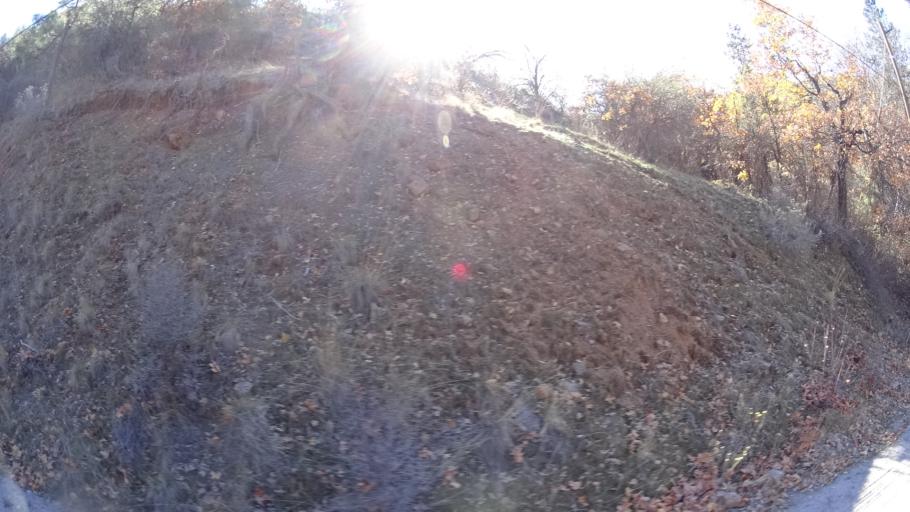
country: US
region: California
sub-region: Siskiyou County
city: Yreka
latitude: 41.8308
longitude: -122.6307
